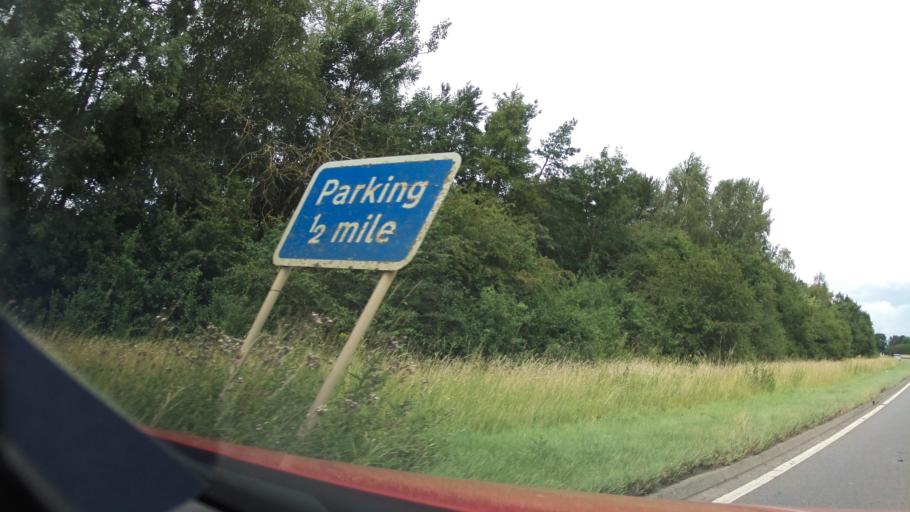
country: GB
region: England
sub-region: Northamptonshire
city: Corby
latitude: 52.4836
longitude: -0.7332
